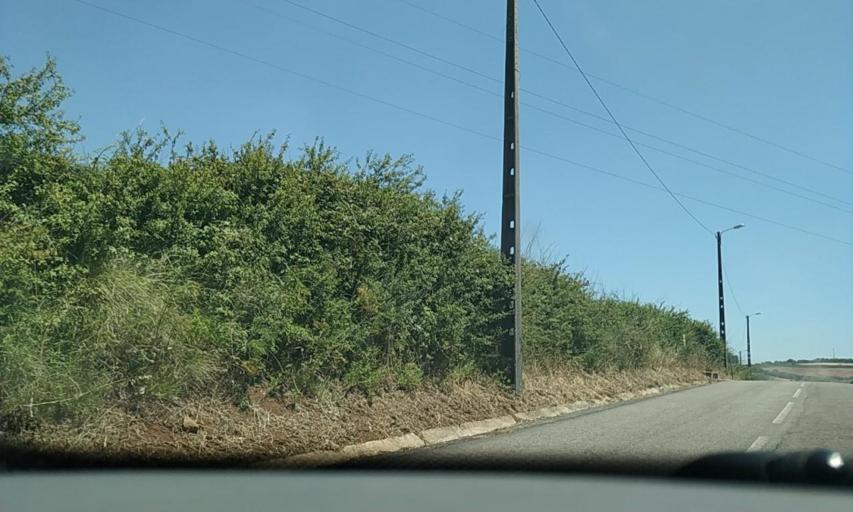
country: PT
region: Lisbon
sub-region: Sintra
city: Pero Pinheiro
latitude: 38.8636
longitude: -9.3117
